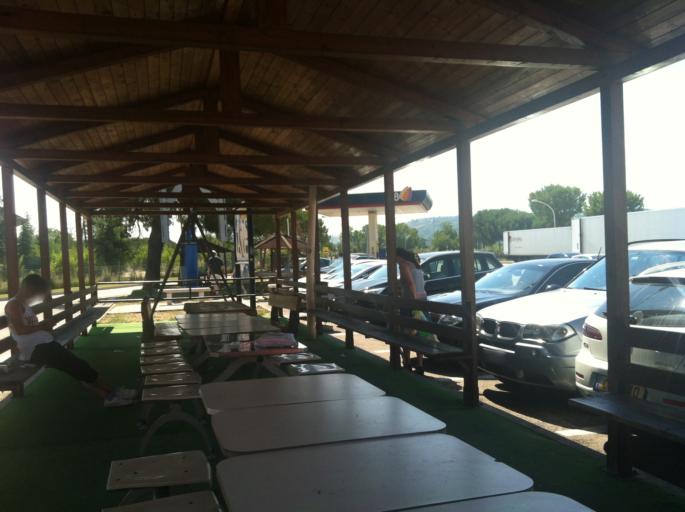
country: IT
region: Abruzzo
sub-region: Provincia di Pescara
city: Manoppello Scalo
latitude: 42.3252
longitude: 14.0875
